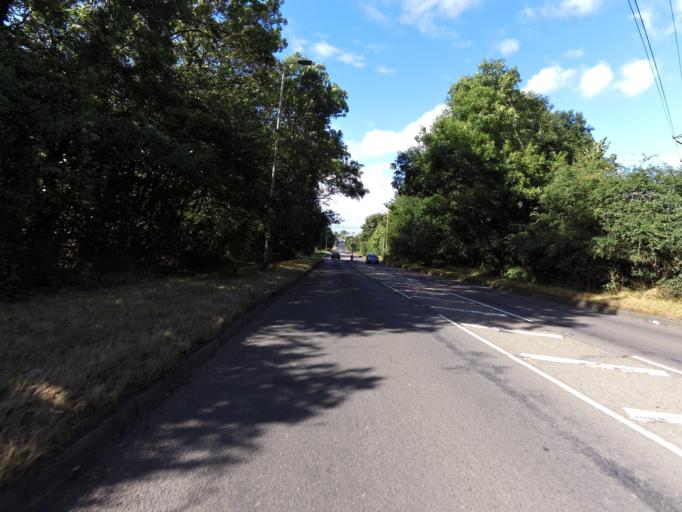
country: GB
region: England
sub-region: Hertfordshire
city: Radlett
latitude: 51.6996
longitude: -0.3261
